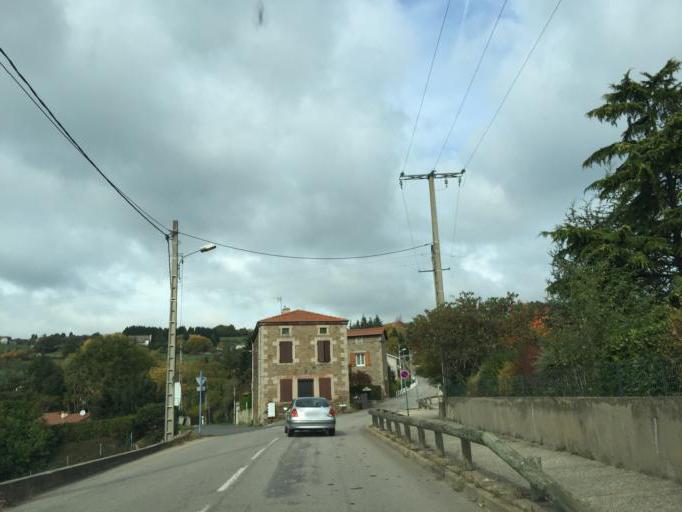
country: FR
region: Rhone-Alpes
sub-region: Departement de la Loire
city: Sorbiers
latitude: 45.4906
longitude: 4.4860
